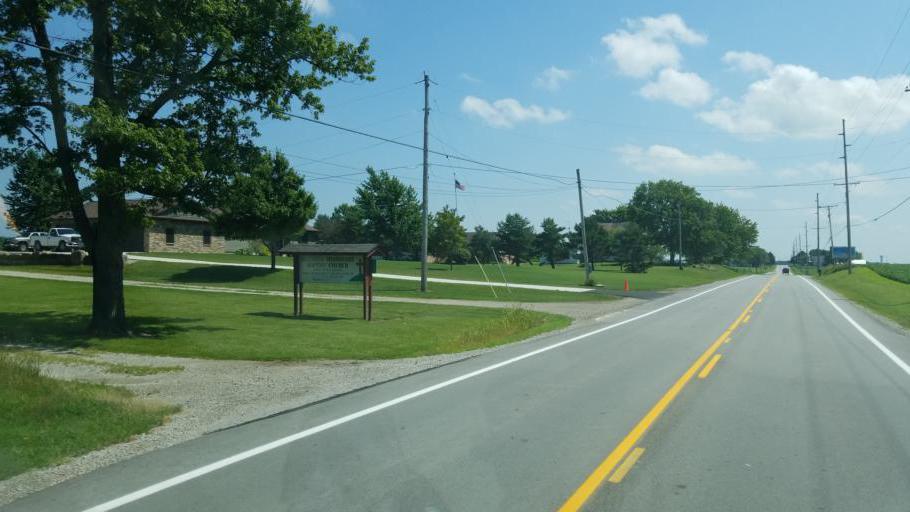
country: US
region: Ohio
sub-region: Huron County
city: Bellevue
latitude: 41.3205
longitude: -82.8300
